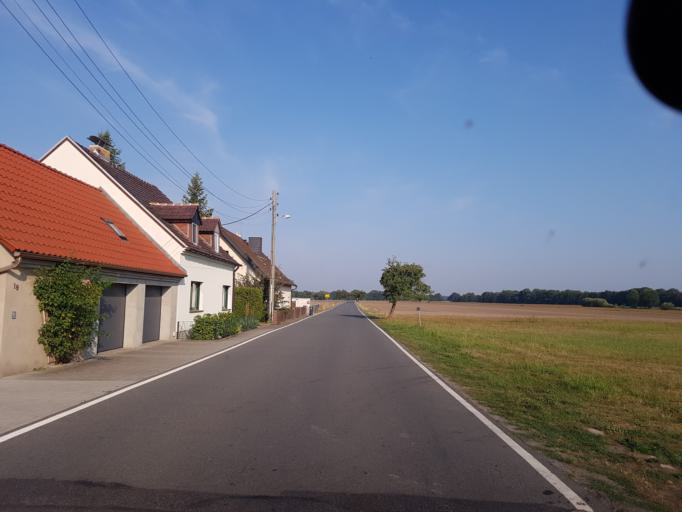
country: DE
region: Brandenburg
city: Finsterwalde
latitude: 51.6669
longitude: 13.7303
